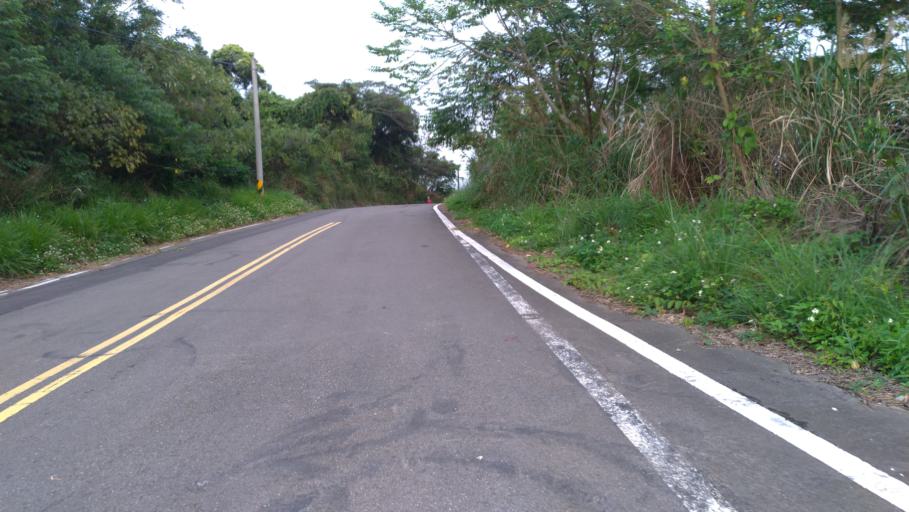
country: TW
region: Taiwan
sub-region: Hsinchu
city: Hsinchu
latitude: 24.7509
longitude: 120.9855
